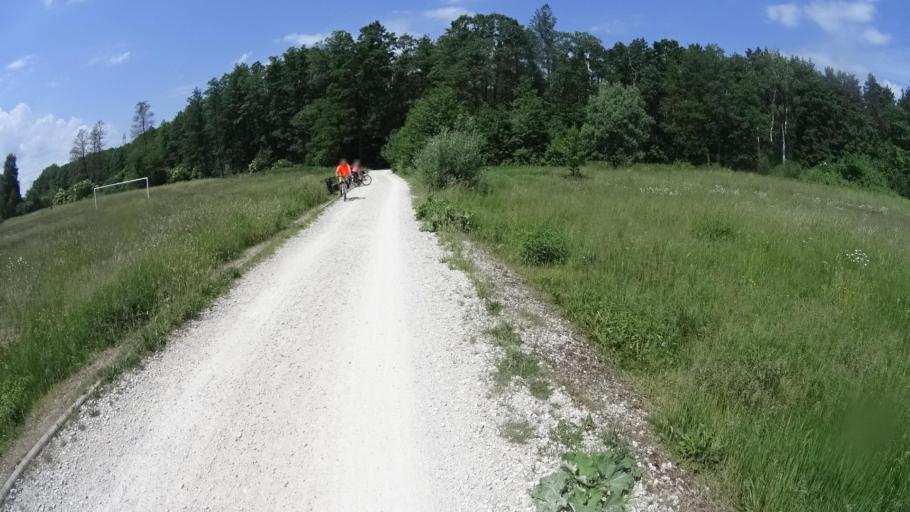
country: PL
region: Masovian Voivodeship
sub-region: Powiat warszawski zachodni
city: Stare Babice
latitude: 52.2705
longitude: 20.8428
